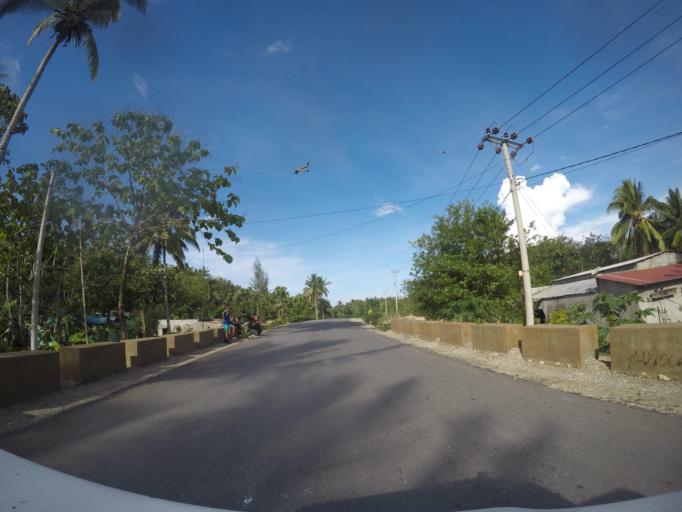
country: TL
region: Baucau
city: Baucau
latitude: -8.4994
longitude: 126.4507
